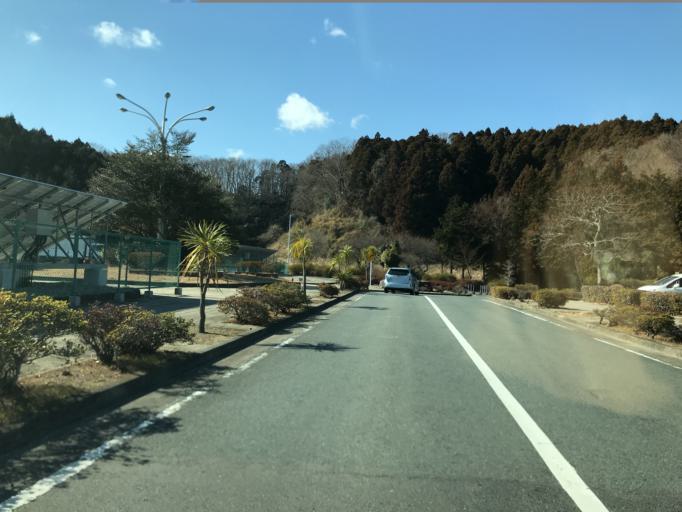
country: JP
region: Fukushima
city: Iwaki
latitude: 37.0324
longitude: 140.8965
